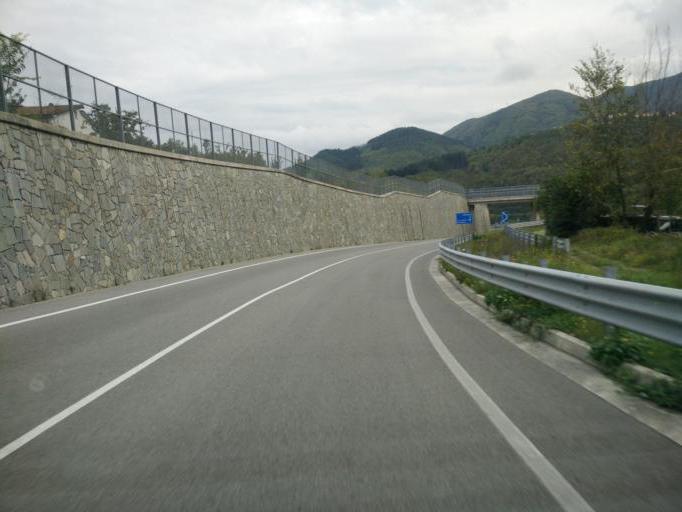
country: IT
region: Tuscany
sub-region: Provincia di Lucca
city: Piazza al Serchio-San Michele
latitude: 44.1802
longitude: 10.3098
